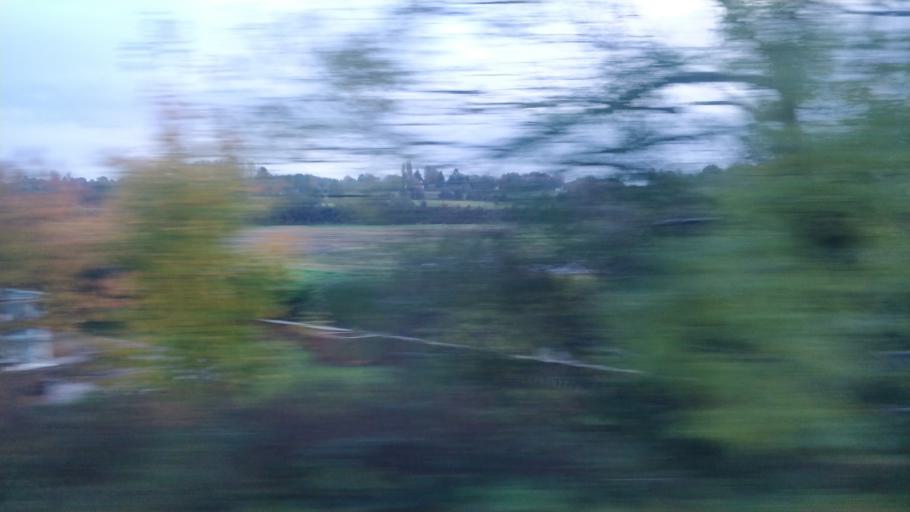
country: GB
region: England
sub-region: Lancashire
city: Parbold
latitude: 53.5920
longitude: -2.7769
